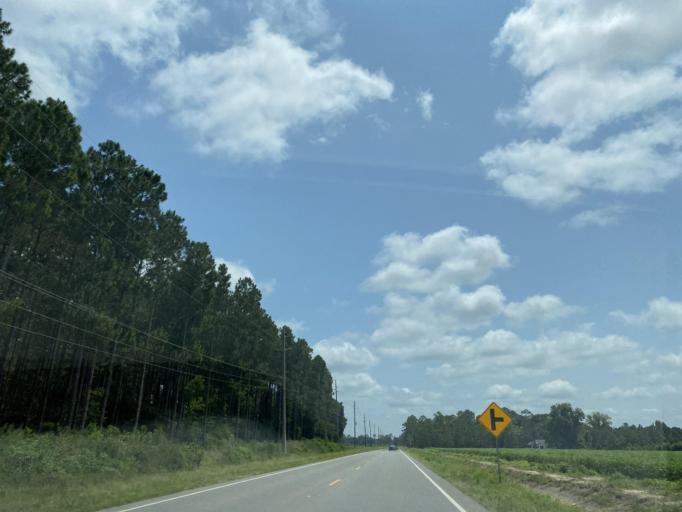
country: US
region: Georgia
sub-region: Jeff Davis County
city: Hazlehurst
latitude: 31.8301
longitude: -82.5748
